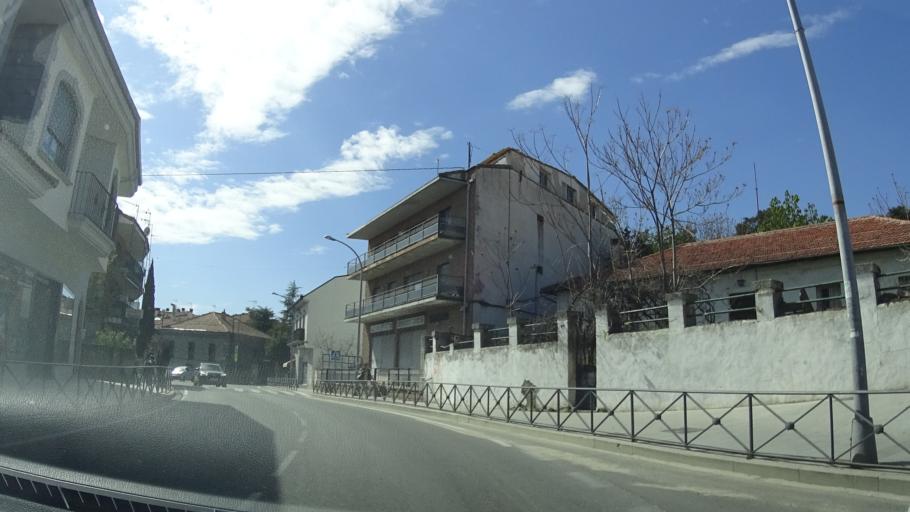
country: ES
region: Madrid
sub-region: Provincia de Madrid
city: Hoyo de Manzanares
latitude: 40.6217
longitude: -3.9069
